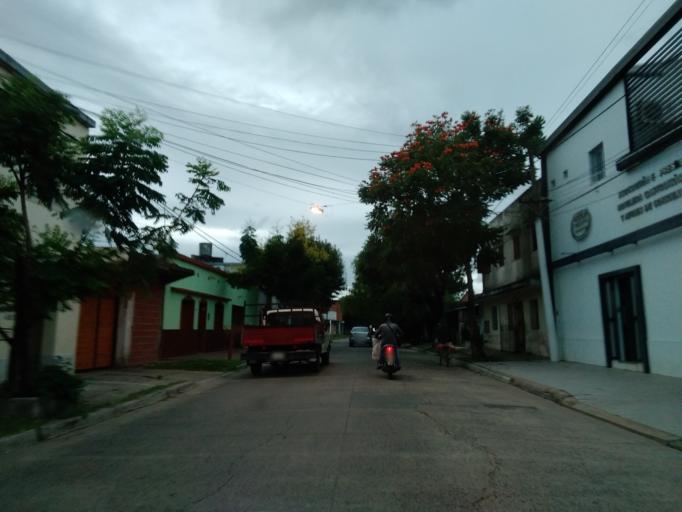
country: AR
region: Corrientes
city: Corrientes
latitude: -27.4785
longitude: -58.8222
